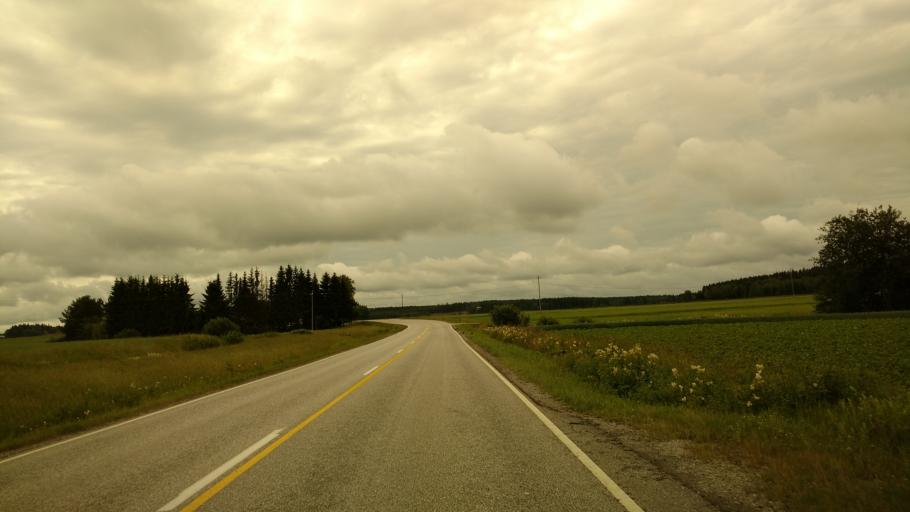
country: FI
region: Varsinais-Suomi
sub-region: Salo
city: Kuusjoki
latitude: 60.4746
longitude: 23.1585
